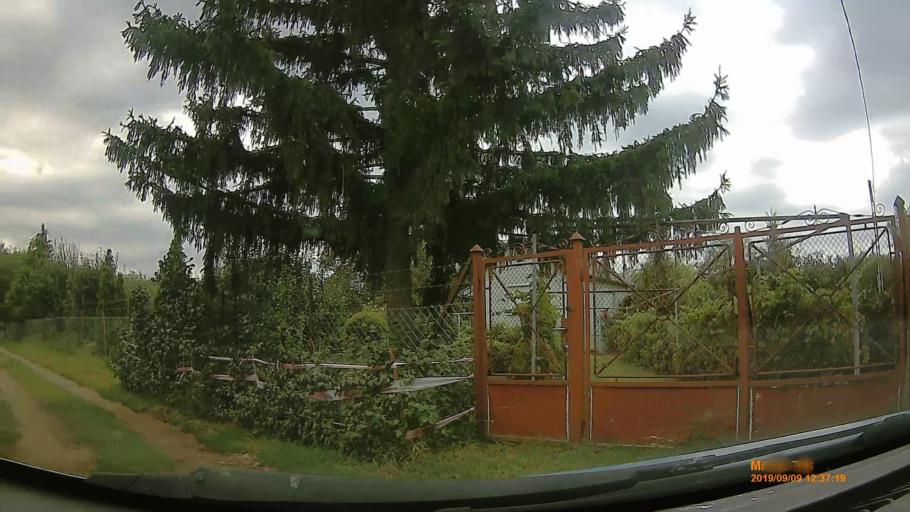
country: HU
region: Szabolcs-Szatmar-Bereg
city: Nyirpazony
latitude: 47.9975
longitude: 21.8077
